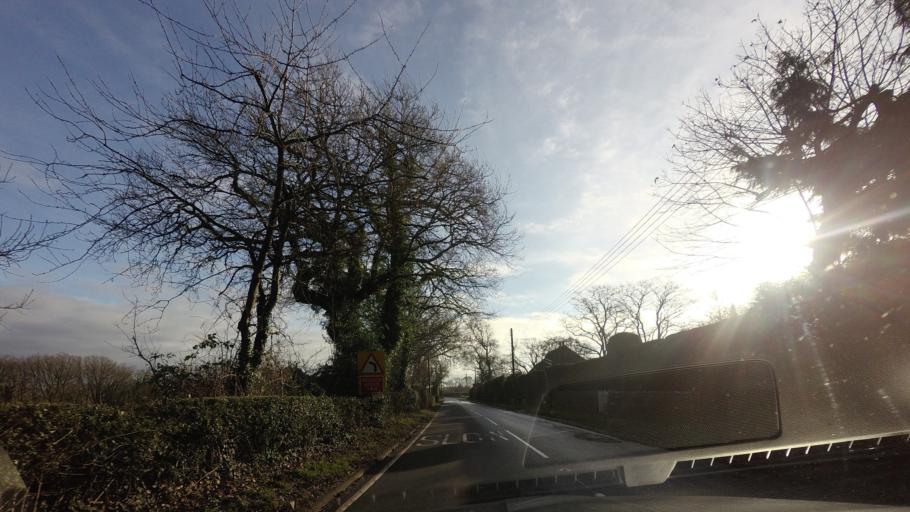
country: GB
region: England
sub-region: East Sussex
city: Bexhill-on-Sea
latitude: 50.8759
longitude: 0.4306
